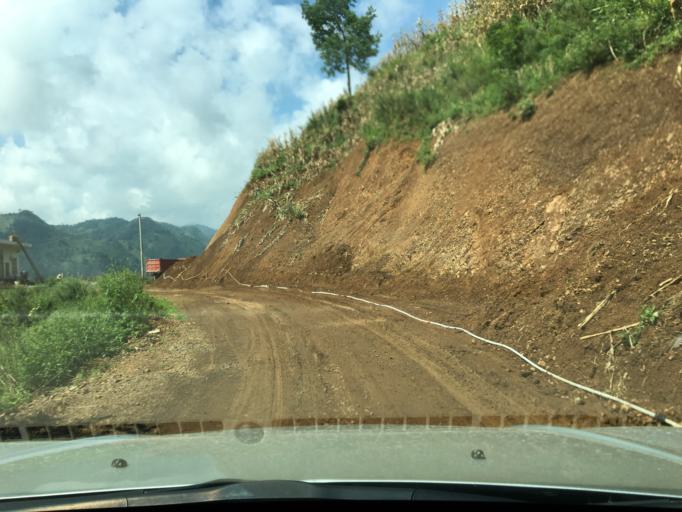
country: CN
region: Guizhou Sheng
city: Liupanshui
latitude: 25.9077
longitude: 105.1080
